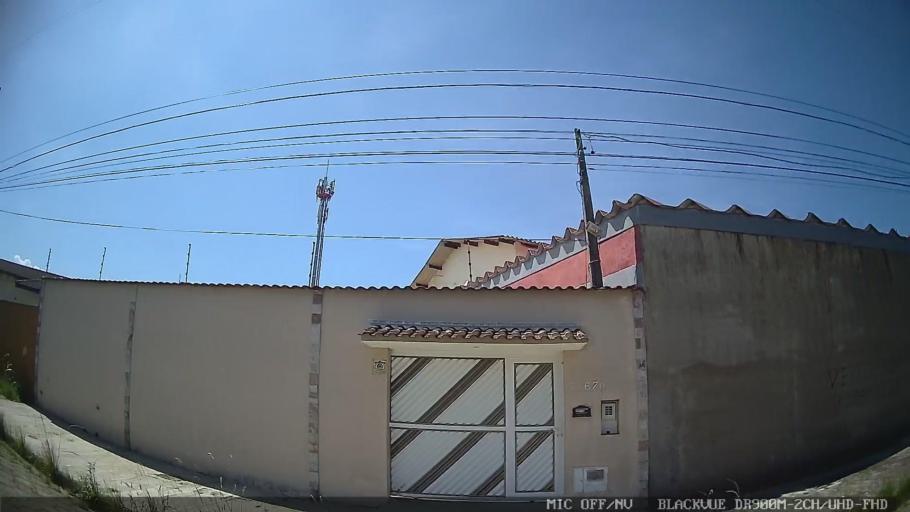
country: BR
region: Sao Paulo
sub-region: Peruibe
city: Peruibe
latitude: -24.3034
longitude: -46.9807
